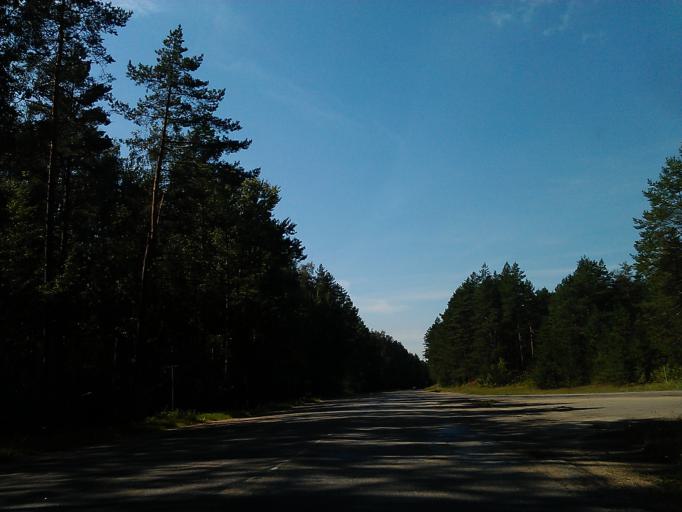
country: LV
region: Salaspils
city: Salaspils
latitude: 56.9417
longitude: 24.4098
